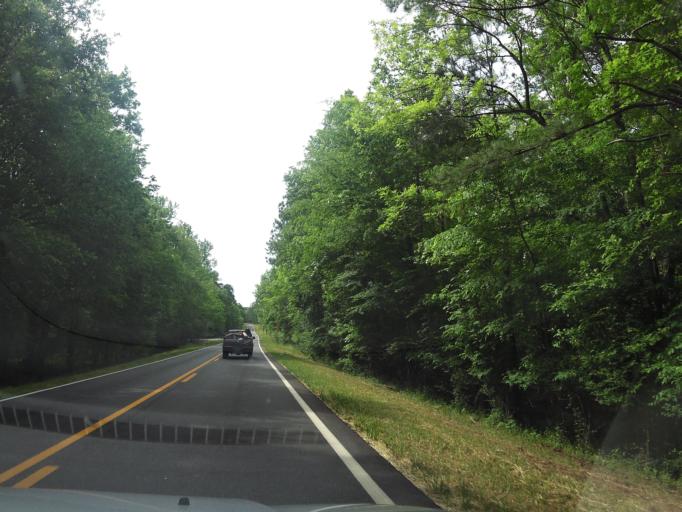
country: US
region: Georgia
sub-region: McDuffie County
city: Thomson
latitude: 33.5314
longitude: -82.4850
